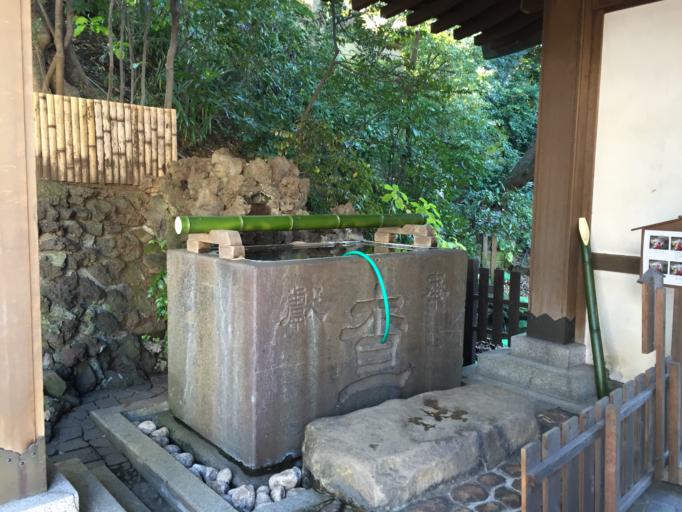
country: JP
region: Kanagawa
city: Yokohama
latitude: 35.4506
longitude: 139.6260
